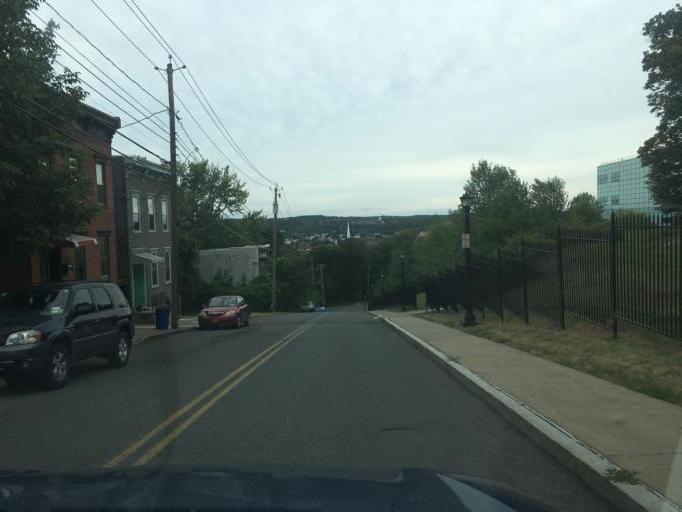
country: US
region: New York
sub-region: Rensselaer County
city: Troy
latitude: 42.7278
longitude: -73.6829
